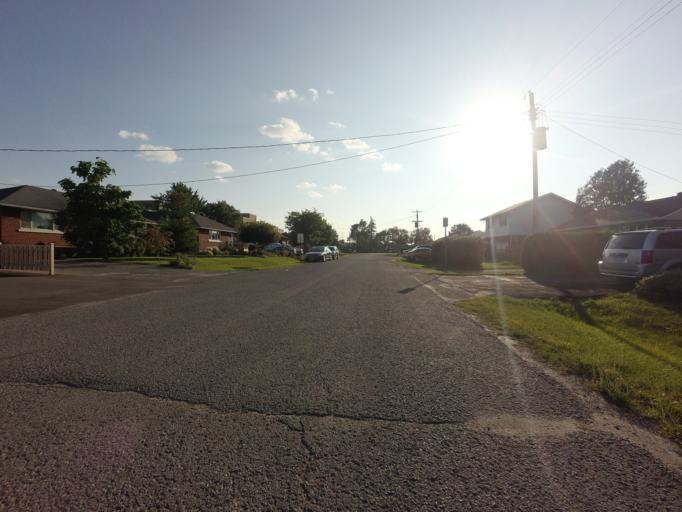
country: CA
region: Ontario
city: Bells Corners
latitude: 45.3439
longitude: -75.7545
